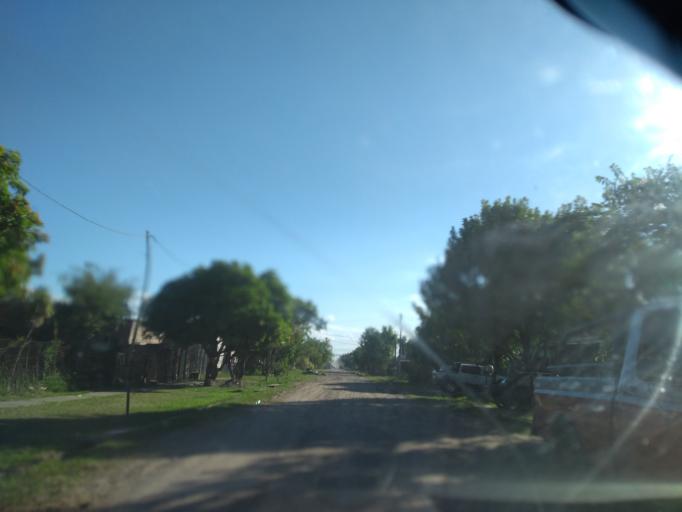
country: AR
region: Chaco
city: Resistencia
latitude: -27.4757
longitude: -58.9692
